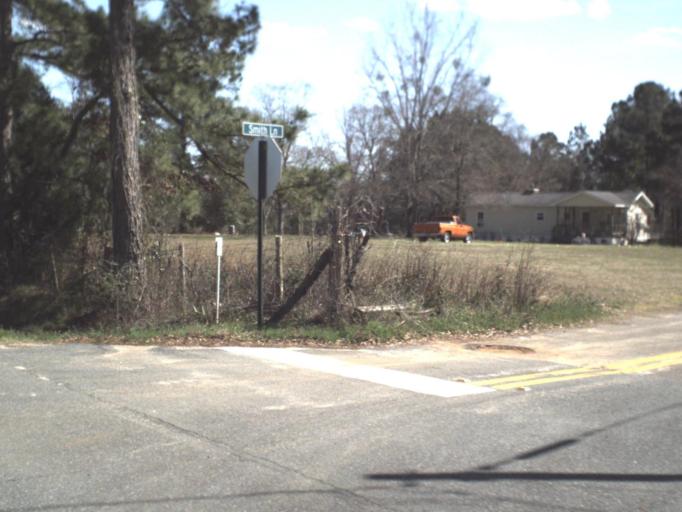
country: US
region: Florida
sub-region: Gadsden County
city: Chattahoochee
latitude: 30.7021
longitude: -84.7841
